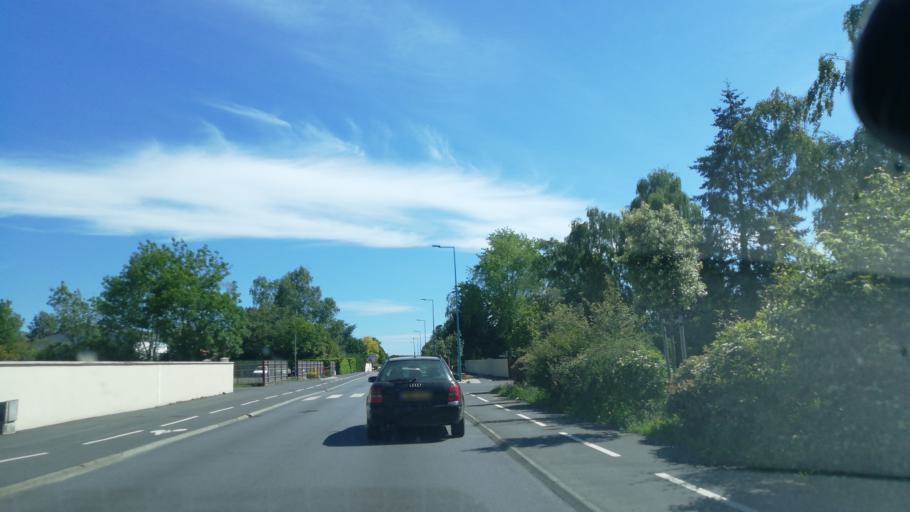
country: FR
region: Poitou-Charentes
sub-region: Departement des Deux-Sevres
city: Moncoutant
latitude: 46.7273
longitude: -0.5848
